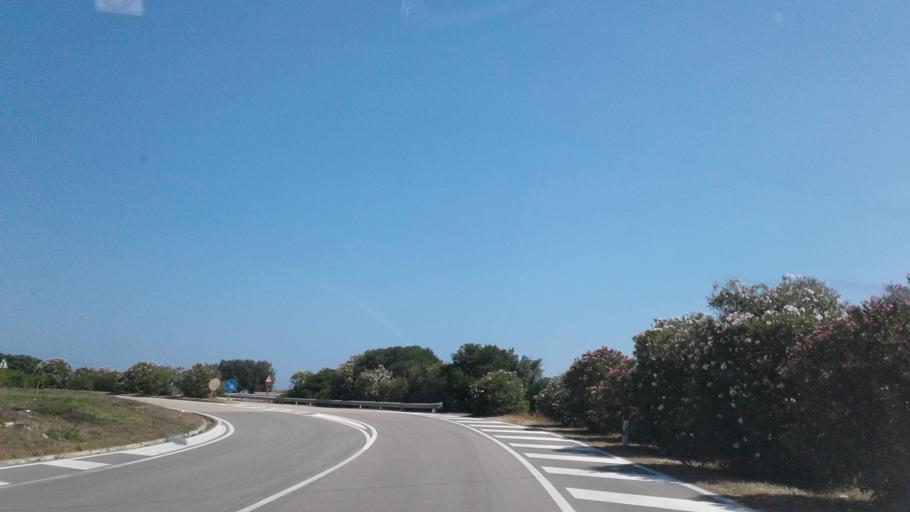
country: IT
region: Sardinia
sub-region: Provincia di Olbia-Tempio
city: Palau
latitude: 41.1624
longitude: 9.3129
